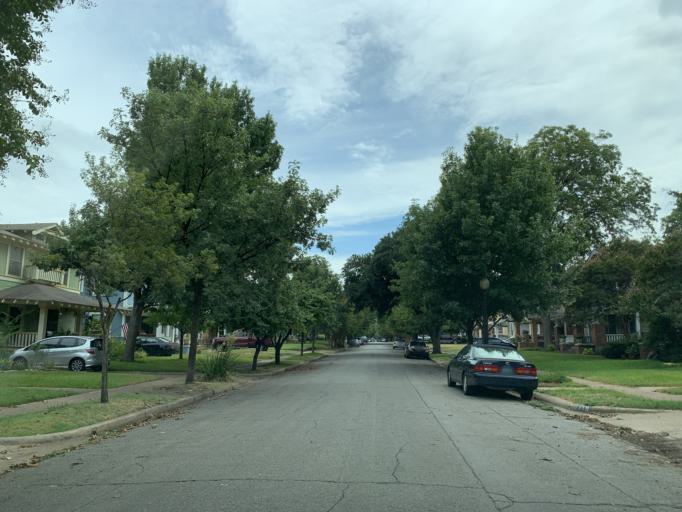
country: US
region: Texas
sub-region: Dallas County
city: Cockrell Hill
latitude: 32.7446
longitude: -96.8478
